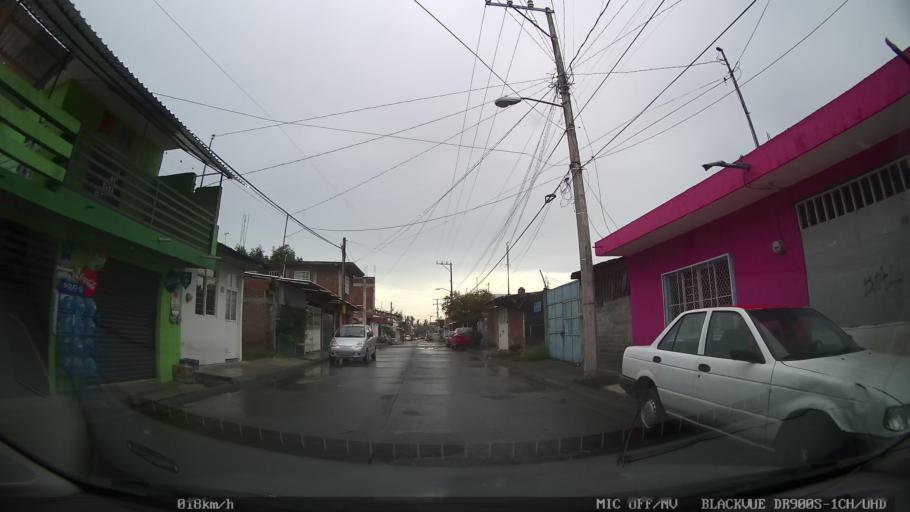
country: MX
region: Michoacan
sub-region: Uruapan
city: Santa Rosa (Santa Barbara)
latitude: 19.4019
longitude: -102.0261
